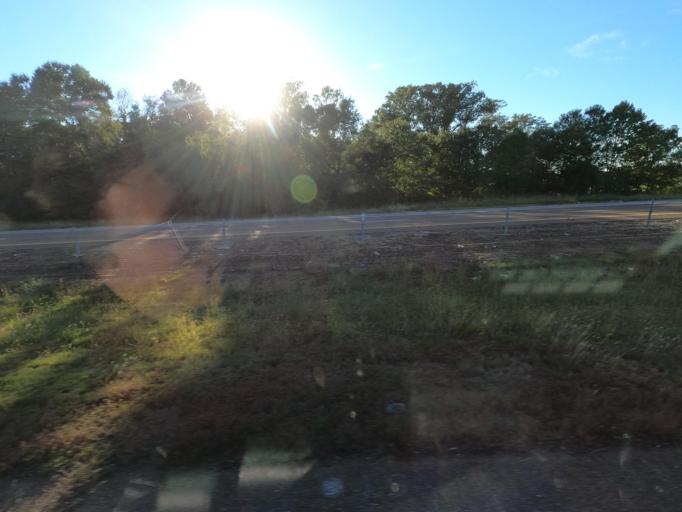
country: US
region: Tennessee
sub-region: Shelby County
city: Arlington
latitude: 35.2777
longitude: -89.6797
